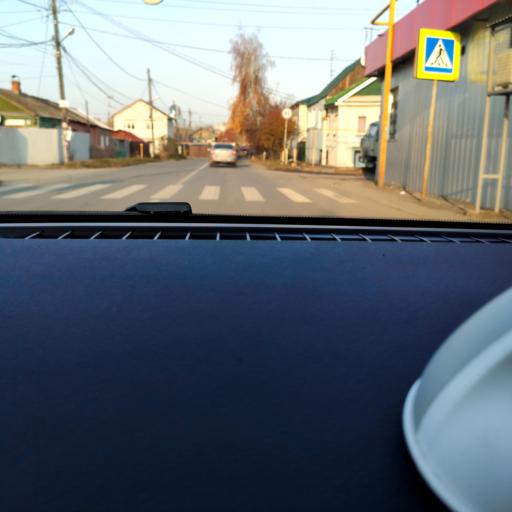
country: RU
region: Samara
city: Samara
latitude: 53.1819
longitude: 50.1347
